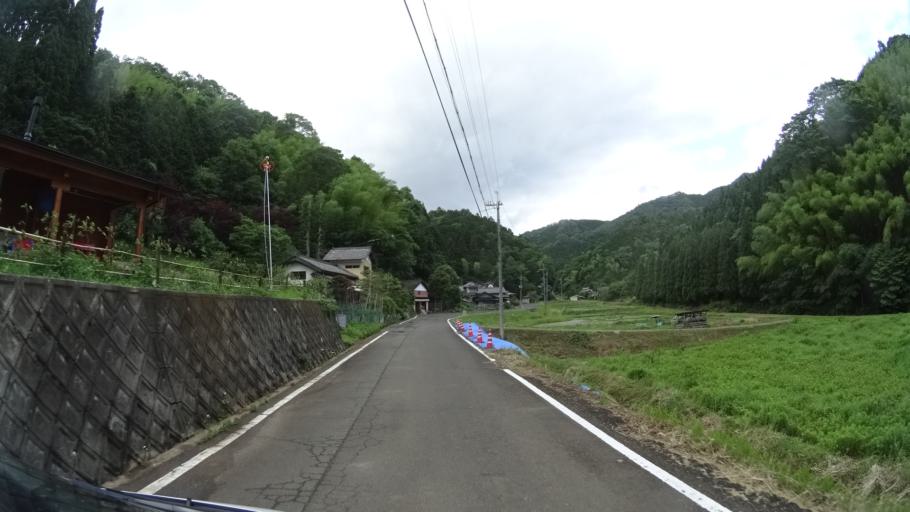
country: JP
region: Kyoto
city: Ayabe
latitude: 35.3874
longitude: 135.2106
